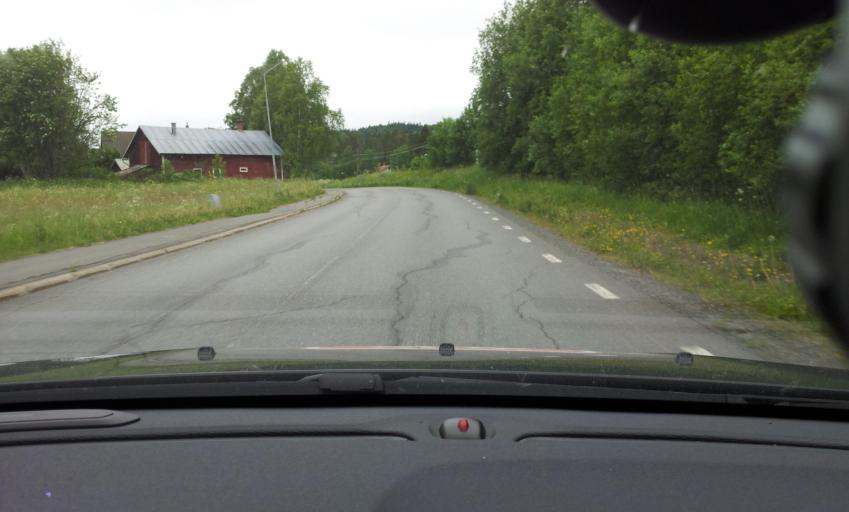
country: SE
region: Jaemtland
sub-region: Are Kommun
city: Jarpen
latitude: 63.3080
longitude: 13.6568
